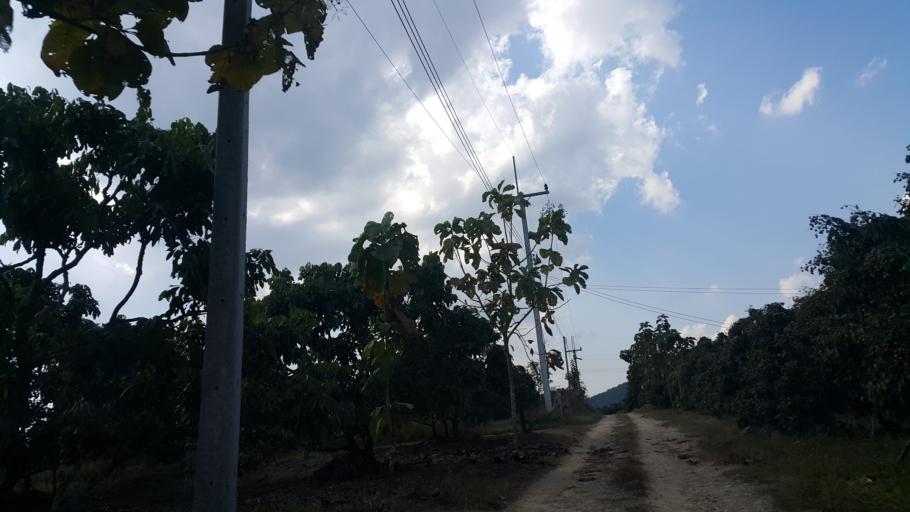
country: TH
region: Lamphun
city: Ban Thi
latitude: 18.5956
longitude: 99.1605
